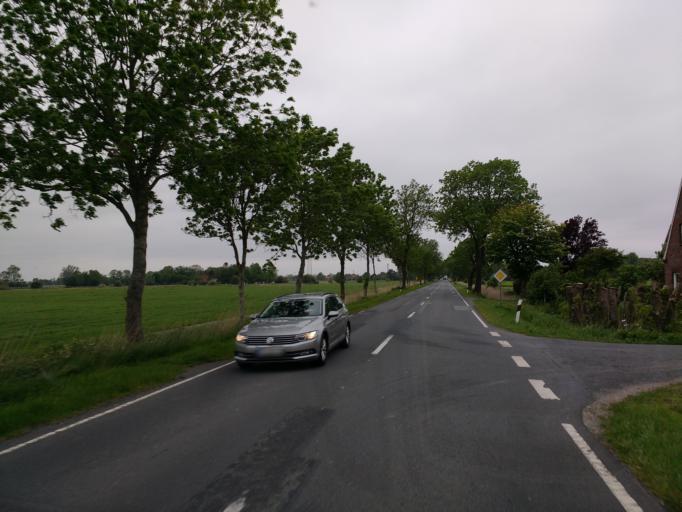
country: DE
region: Lower Saxony
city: Jever
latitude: 53.6533
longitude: 7.9171
